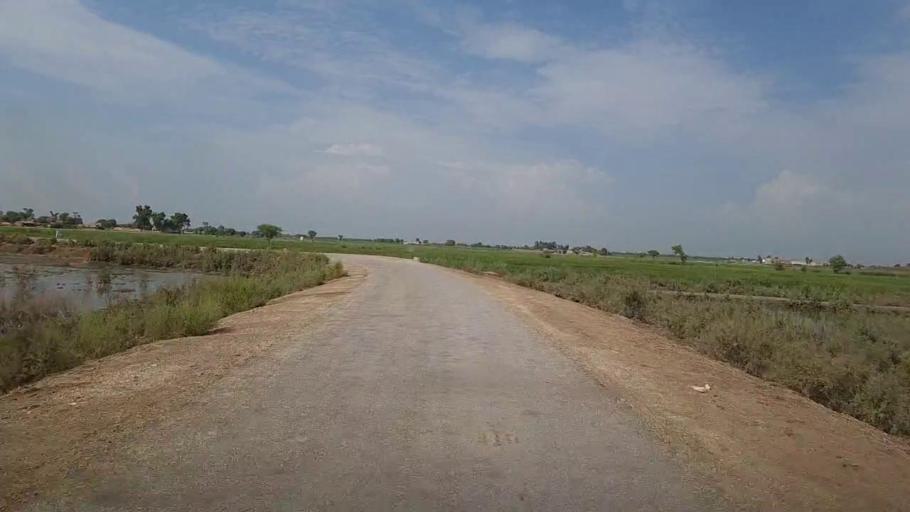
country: PK
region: Sindh
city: Thul
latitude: 28.2884
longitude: 68.8235
